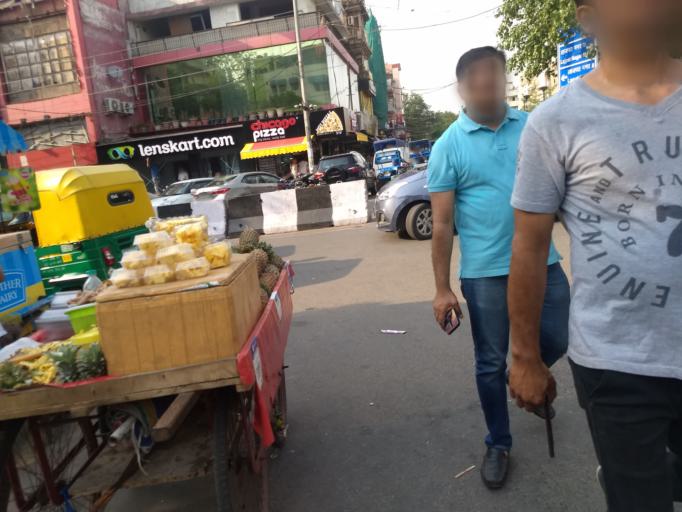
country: IN
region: NCT
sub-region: New Delhi
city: New Delhi
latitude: 28.5705
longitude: 77.2399
